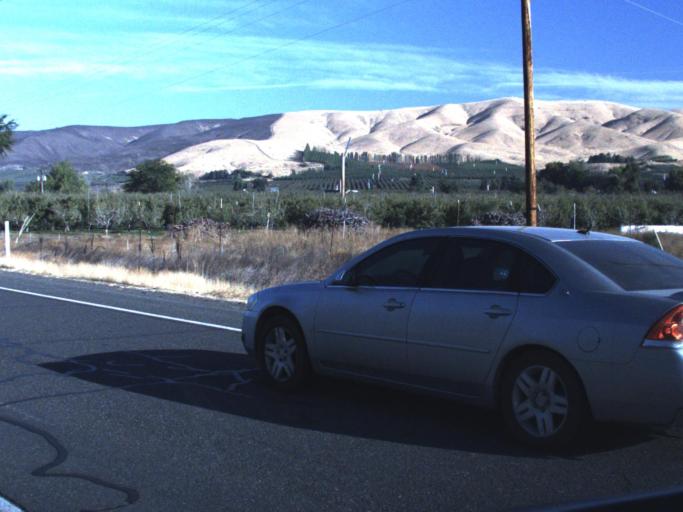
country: US
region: Washington
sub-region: Yakima County
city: Wapato
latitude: 46.4753
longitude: -120.4010
